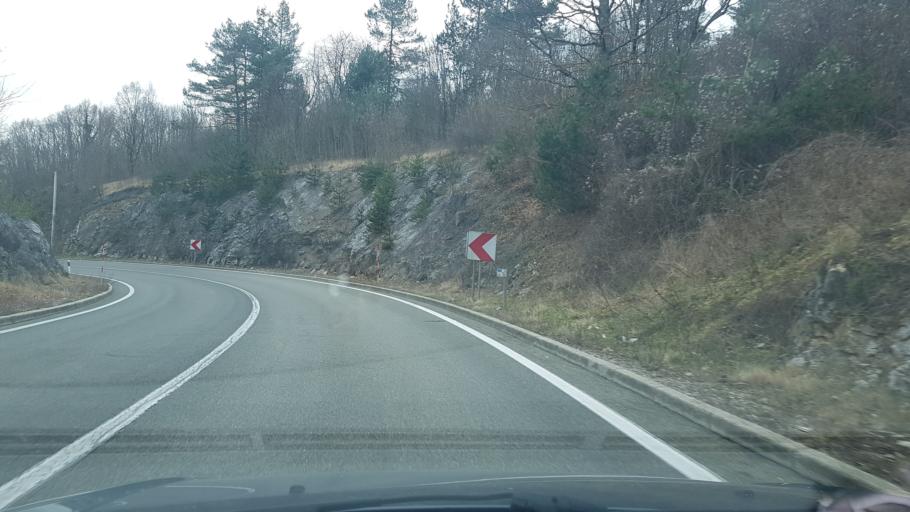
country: SI
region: Ilirska Bistrica
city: Ilirska Bistrica
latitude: 45.4809
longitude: 14.2396
